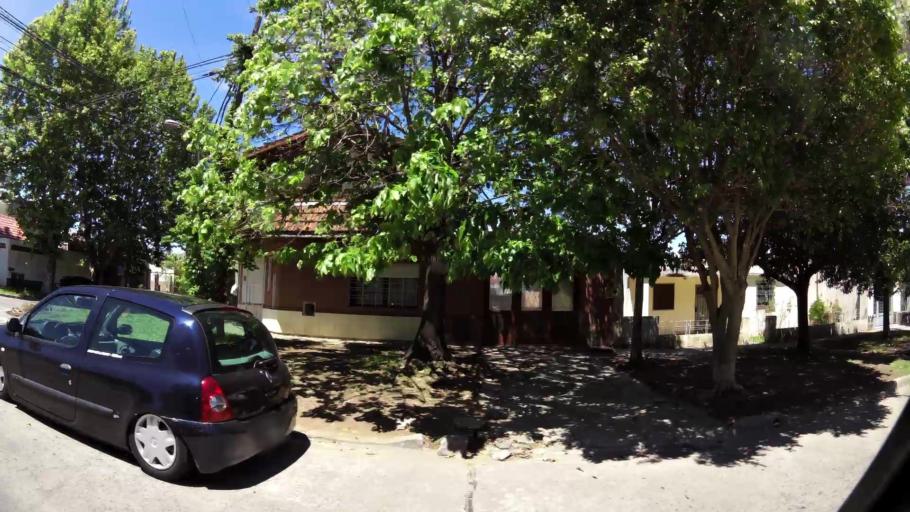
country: AR
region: Buenos Aires
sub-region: Partido de Quilmes
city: Quilmes
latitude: -34.7349
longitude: -58.2862
